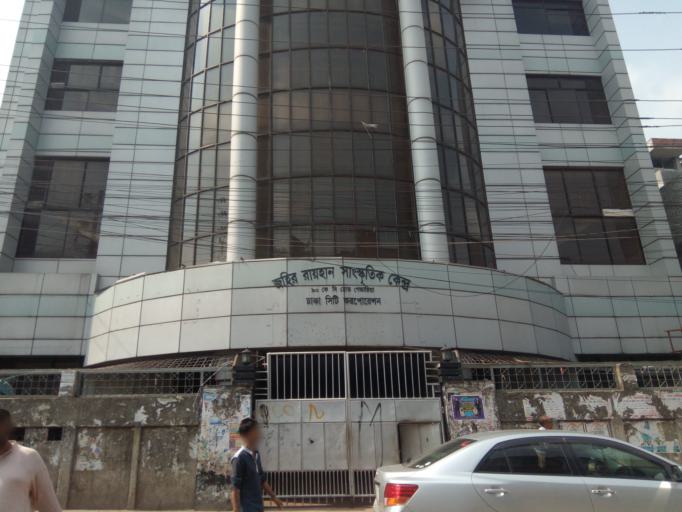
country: BD
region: Dhaka
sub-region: Dhaka
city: Dhaka
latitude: 23.7022
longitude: 90.4198
